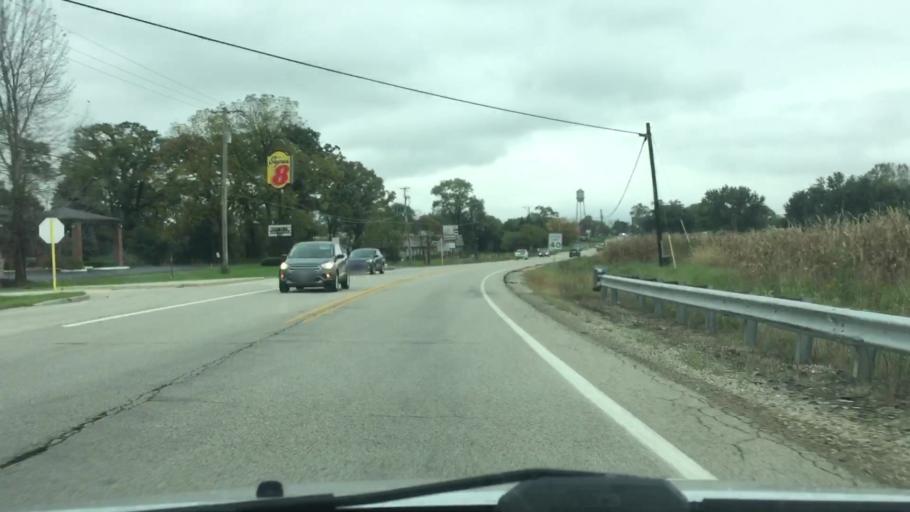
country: US
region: Illinois
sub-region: McHenry County
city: Richmond
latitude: 42.4891
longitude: -88.3063
